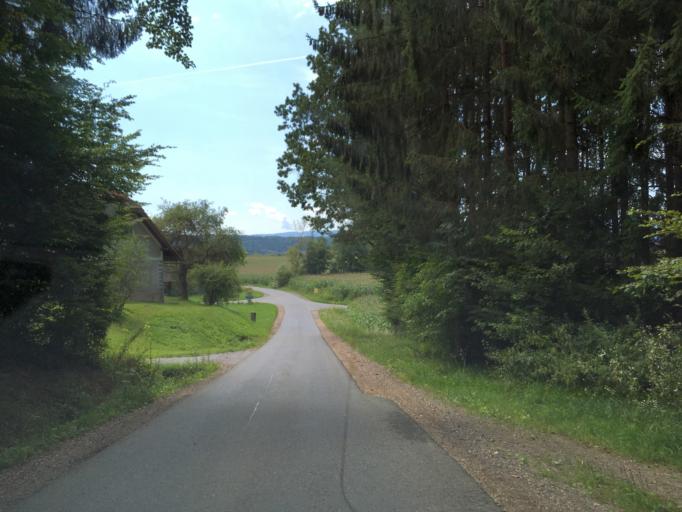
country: AT
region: Styria
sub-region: Politischer Bezirk Leibnitz
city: Pistorf
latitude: 46.7678
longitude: 15.3925
